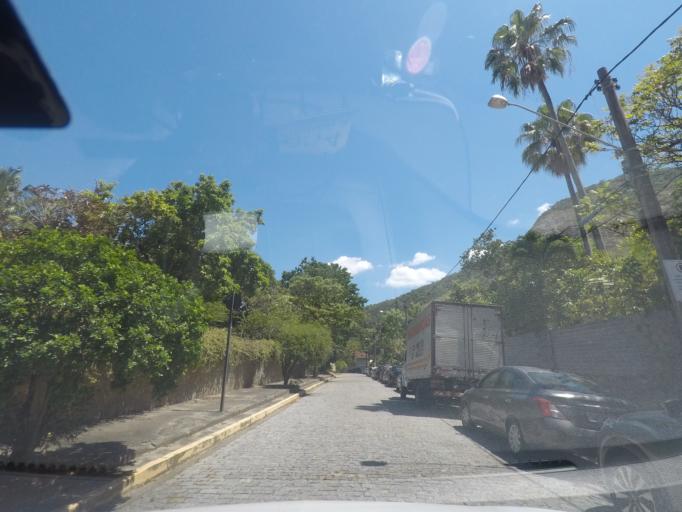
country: BR
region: Rio de Janeiro
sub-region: Niteroi
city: Niteroi
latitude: -22.9745
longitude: -43.0291
